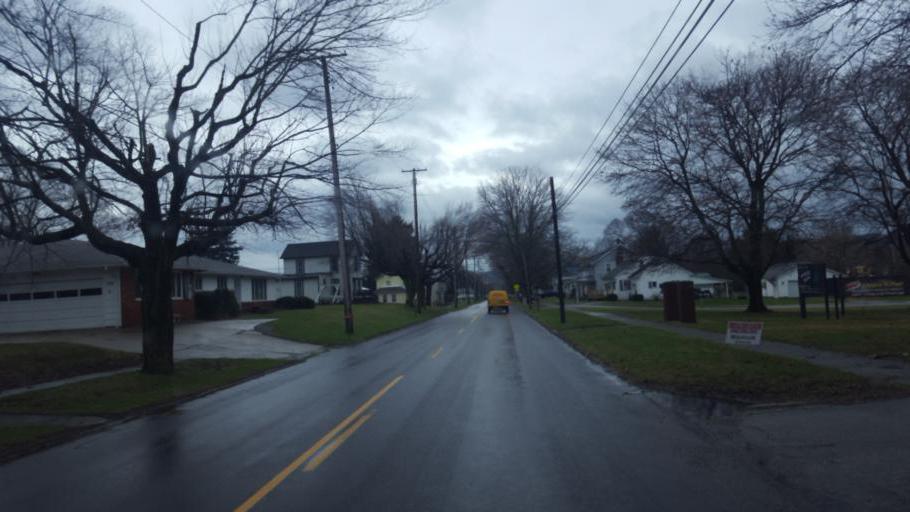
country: US
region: Ohio
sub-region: Ashland County
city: Loudonville
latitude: 40.6602
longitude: -82.3142
